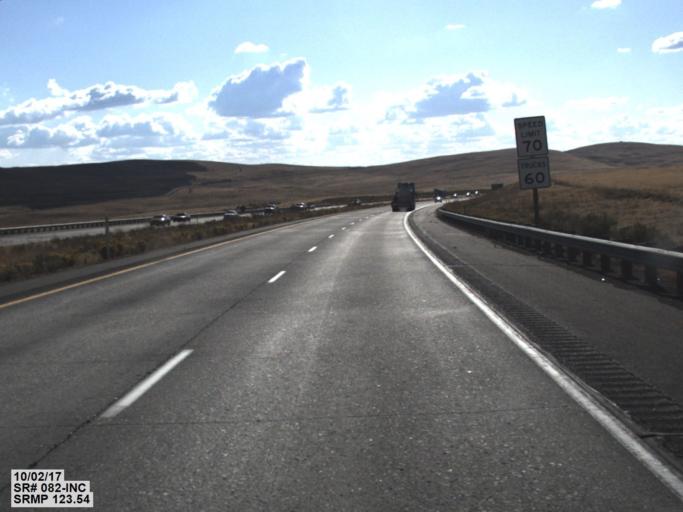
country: US
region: Oregon
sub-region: Umatilla County
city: Umatilla
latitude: 46.0145
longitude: -119.2296
